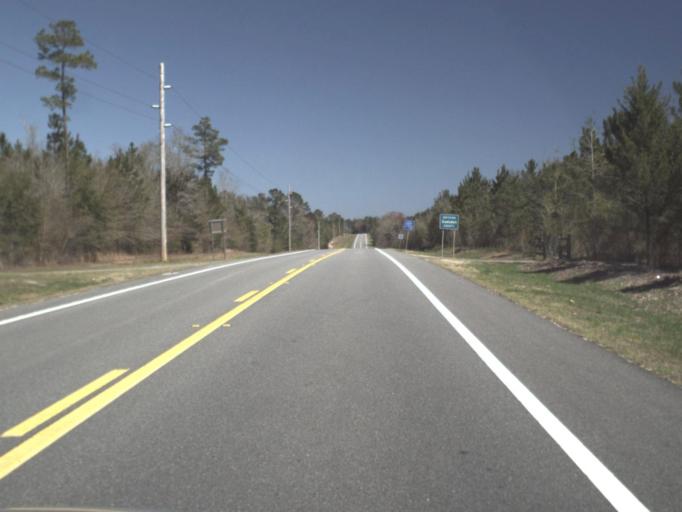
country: US
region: Florida
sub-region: Gadsden County
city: Quincy
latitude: 30.3928
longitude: -84.6809
